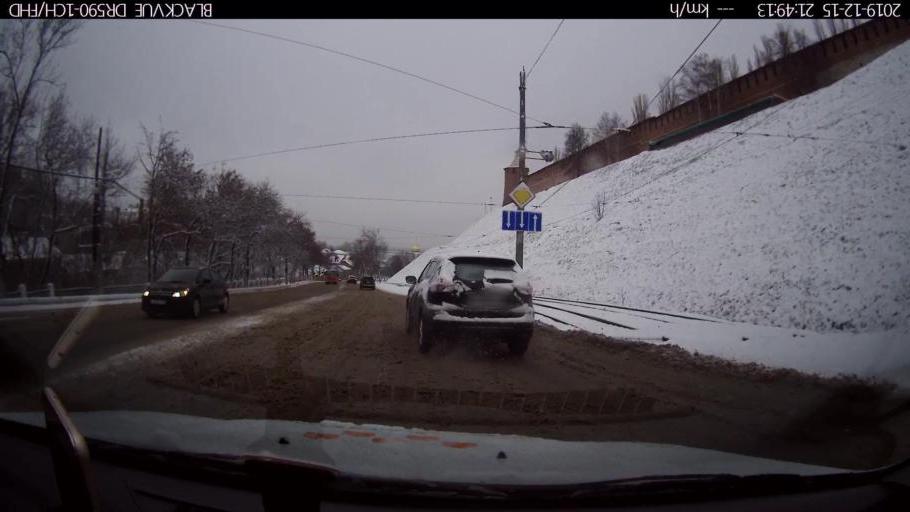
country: RU
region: Nizjnij Novgorod
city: Knyaginino
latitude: 55.8661
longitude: 45.0304
